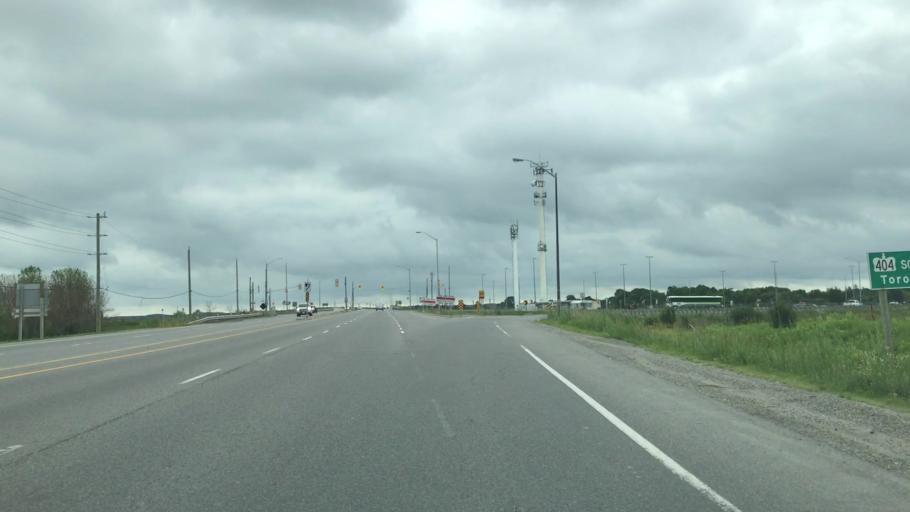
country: CA
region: Ontario
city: Newmarket
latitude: 44.0127
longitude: -79.4112
